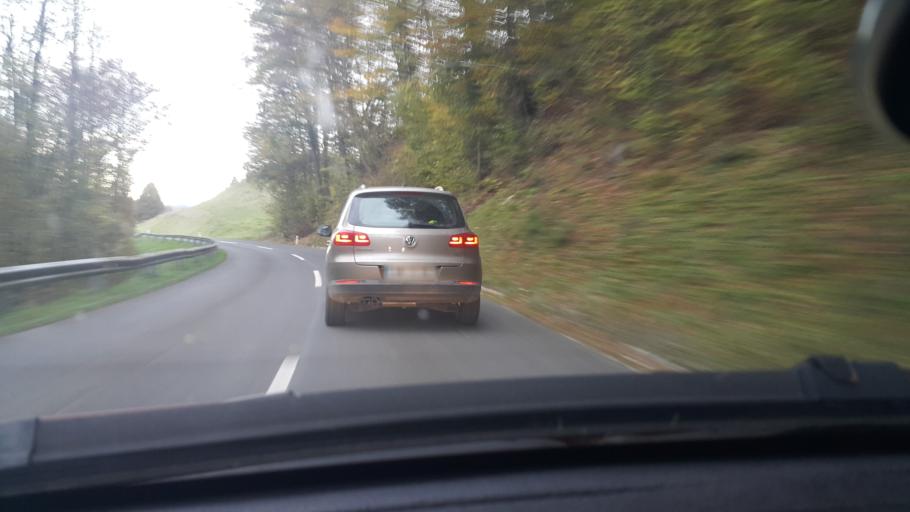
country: AT
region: Styria
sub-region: Politischer Bezirk Leibnitz
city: Leutschach
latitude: 46.6486
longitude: 15.4910
